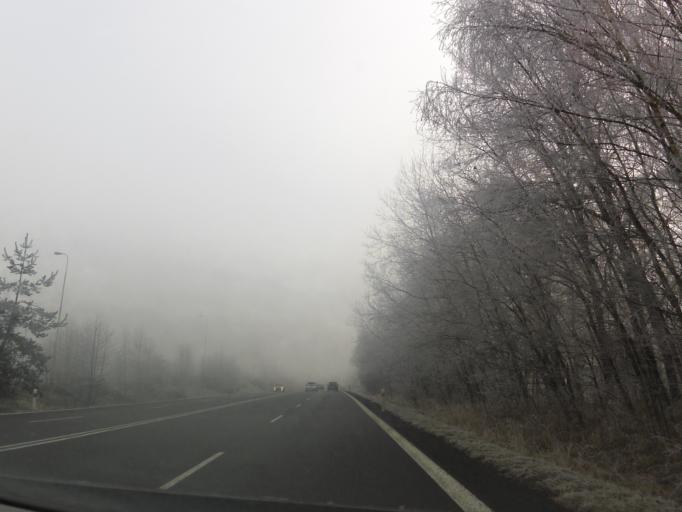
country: DE
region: Bavaria
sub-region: Upper Franconia
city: Schirnding
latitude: 50.0866
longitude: 12.2572
